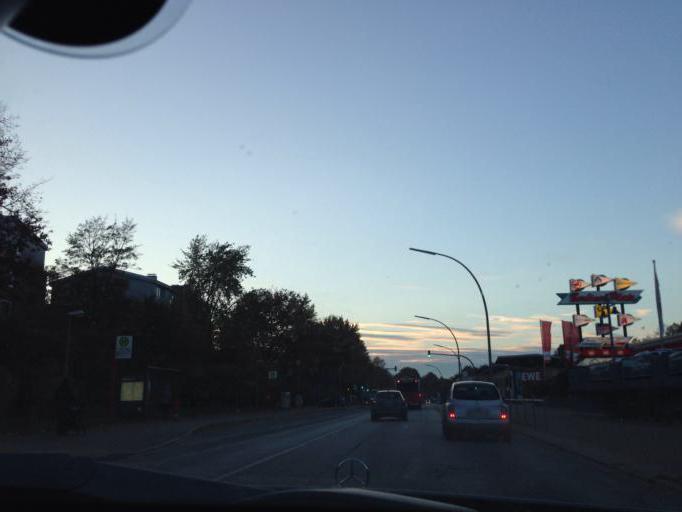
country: DE
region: Schleswig-Holstein
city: Barsbuettel
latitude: 53.5839
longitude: 10.1429
